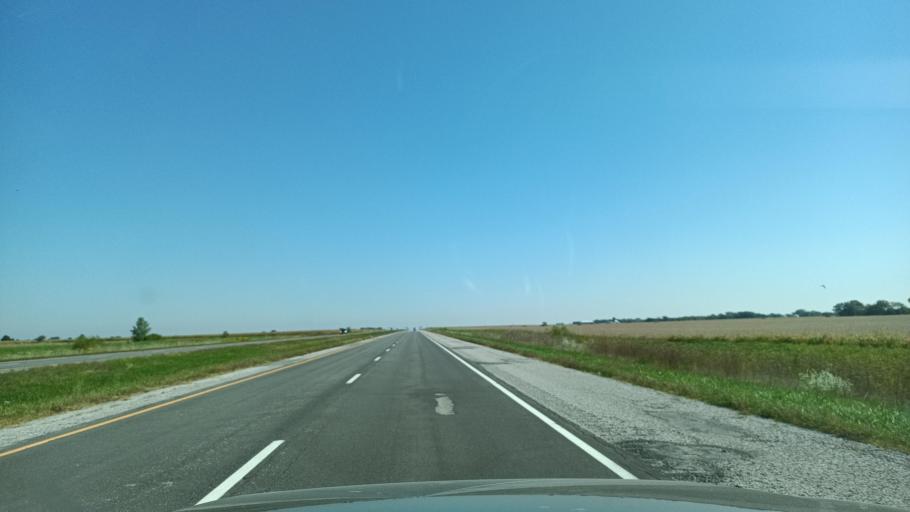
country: US
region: Illinois
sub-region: Adams County
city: Camp Point
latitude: 40.2010
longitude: -91.1495
